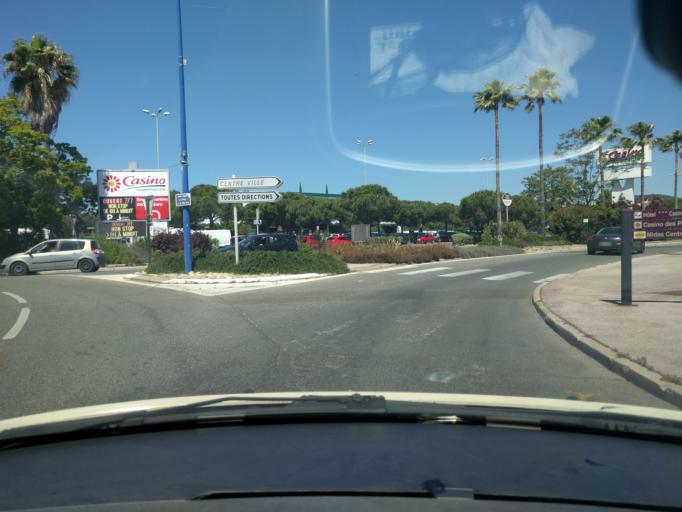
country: FR
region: Provence-Alpes-Cote d'Azur
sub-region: Departement du Var
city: Hyeres
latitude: 43.1067
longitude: 6.1290
